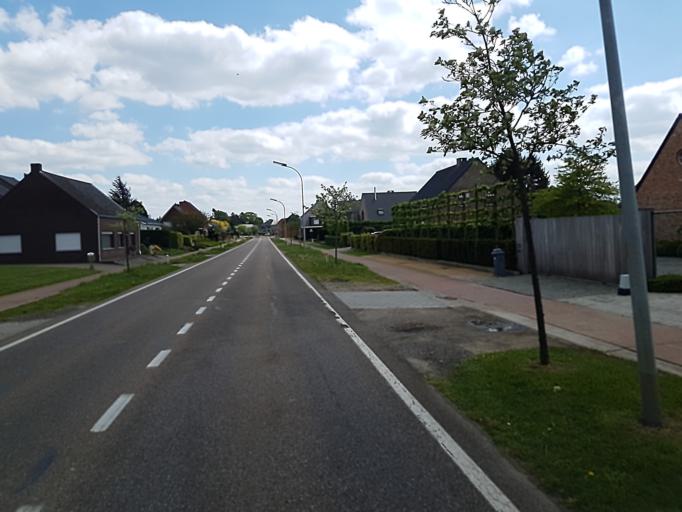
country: BE
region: Flanders
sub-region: Provincie Antwerpen
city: Laakdal
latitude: 51.0675
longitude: 4.9700
